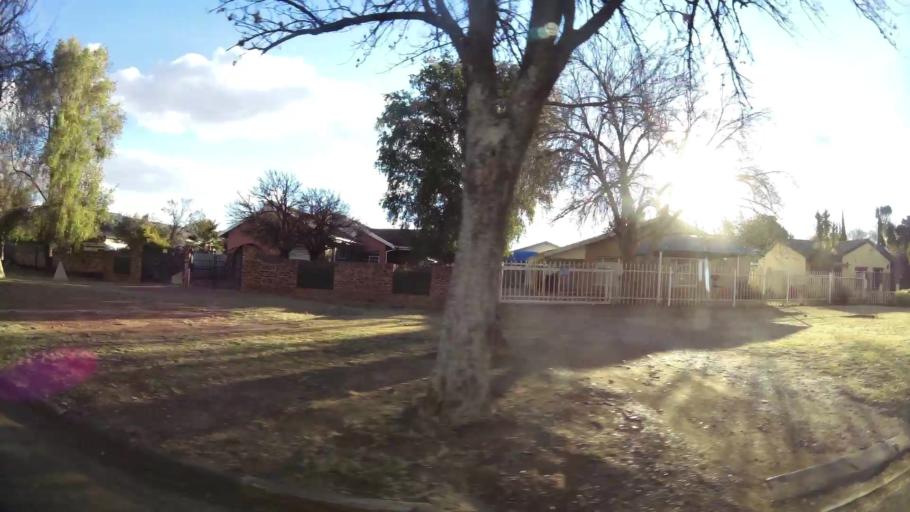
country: ZA
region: North-West
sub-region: Dr Kenneth Kaunda District Municipality
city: Potchefstroom
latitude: -26.7378
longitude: 27.0889
